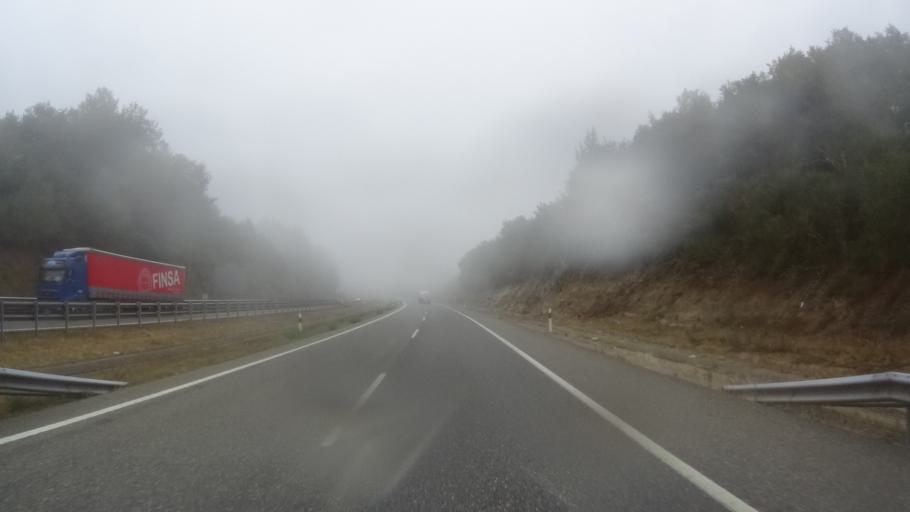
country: ES
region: Galicia
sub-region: Provincia de Lugo
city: Corgo
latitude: 42.9700
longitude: -7.4672
